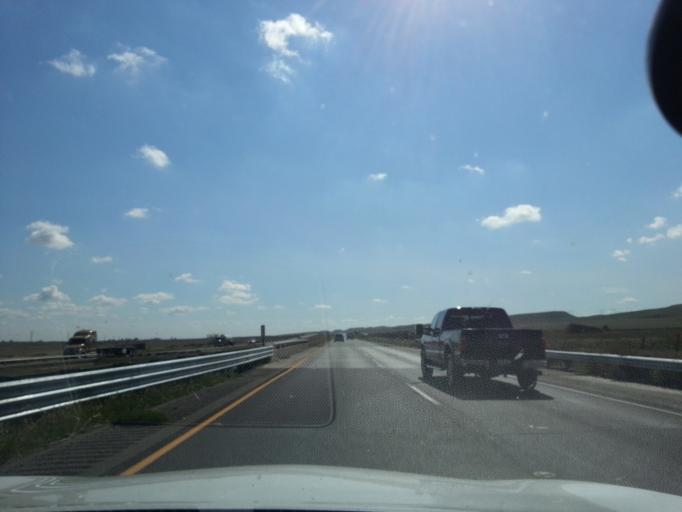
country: US
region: California
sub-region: Fresno County
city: Coalinga
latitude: 36.3527
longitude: -120.3201
